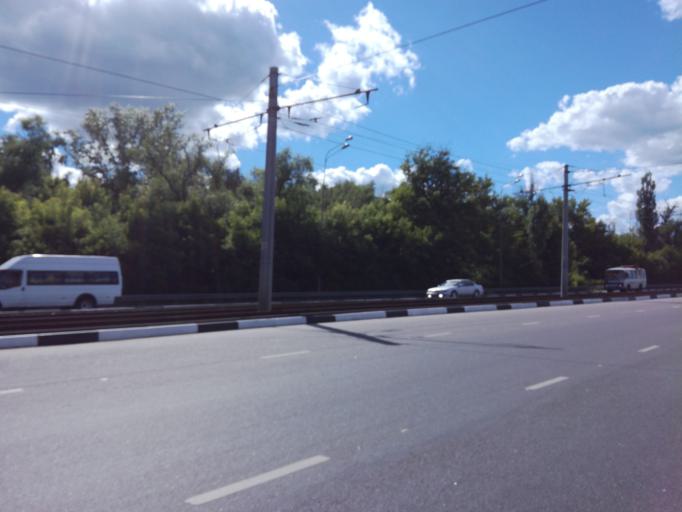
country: RU
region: Kursk
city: Kursk
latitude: 51.7542
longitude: 36.2117
